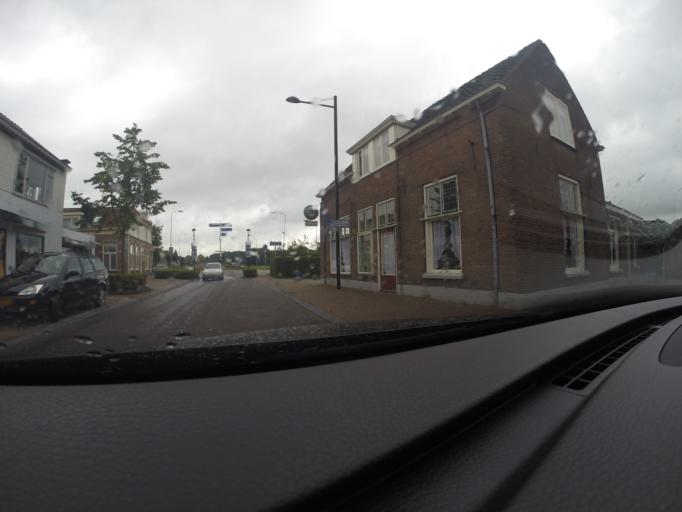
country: NL
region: Gelderland
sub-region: Gemeente Bronckhorst
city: Hengelo
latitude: 52.1037
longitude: 6.3163
